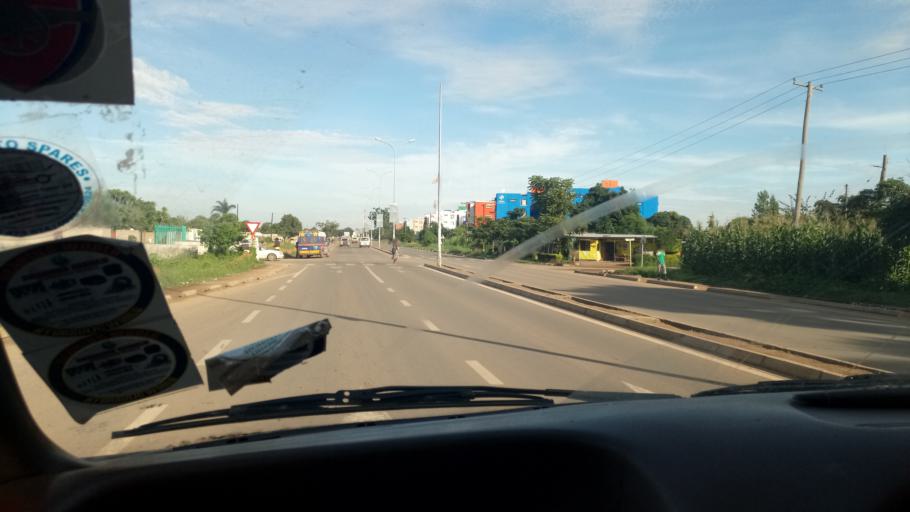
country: ZM
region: Lusaka
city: Lusaka
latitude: -15.4378
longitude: 28.3053
